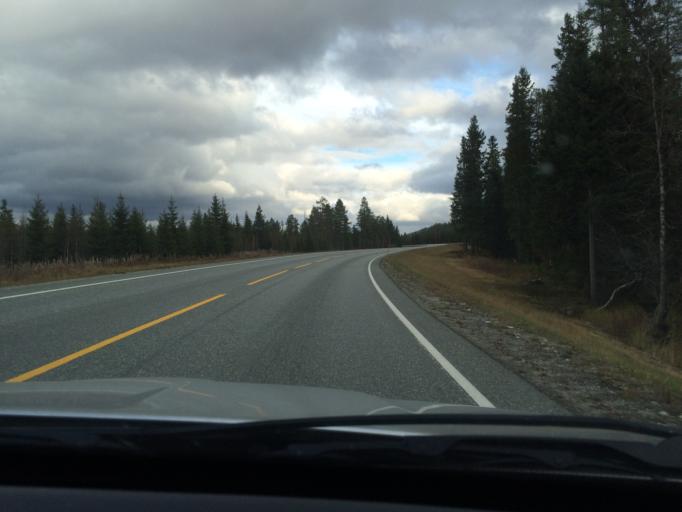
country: NO
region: Nord-Trondelag
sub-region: Namsskogan
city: Namsskogan
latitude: 64.7710
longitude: 12.8725
